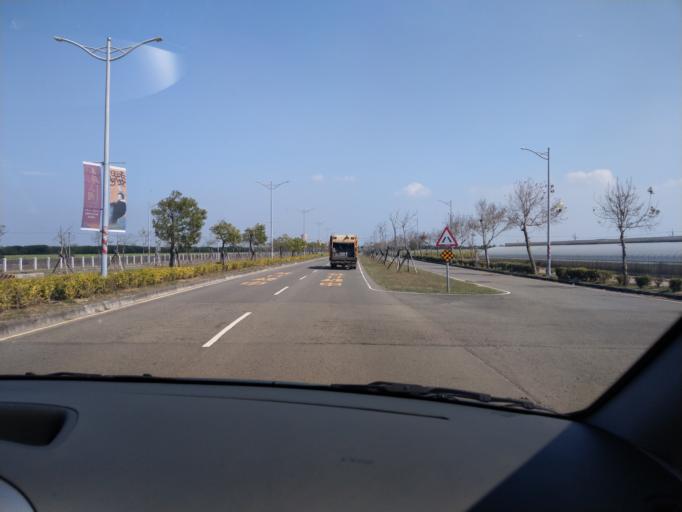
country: TW
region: Taiwan
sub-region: Chiayi
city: Taibao
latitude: 23.4673
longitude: 120.3106
